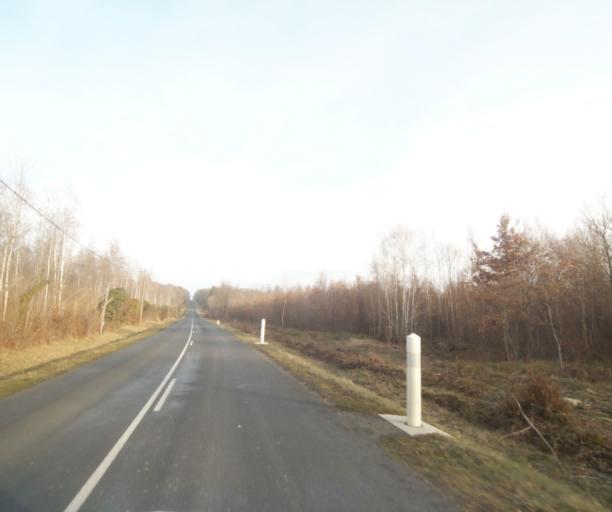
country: FR
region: Champagne-Ardenne
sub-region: Departement de la Haute-Marne
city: Chancenay
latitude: 48.6925
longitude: 4.9458
